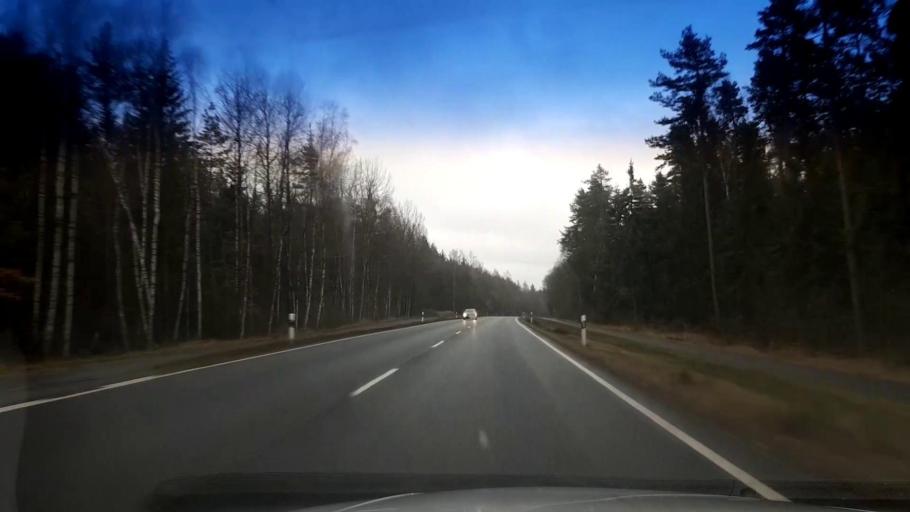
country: DE
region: Bavaria
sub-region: Upper Palatinate
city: Leonberg
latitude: 49.9124
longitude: 12.2980
